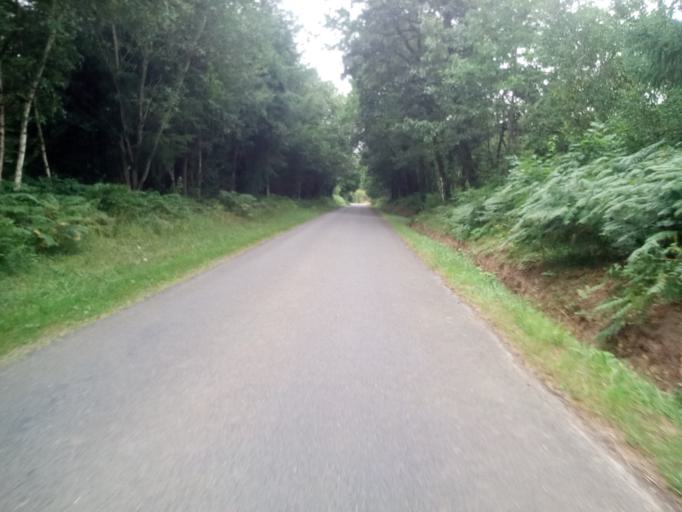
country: FR
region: Lower Normandy
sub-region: Departement du Calvados
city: Clinchamps-sur-Orne
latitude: 49.0294
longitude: -0.3947
